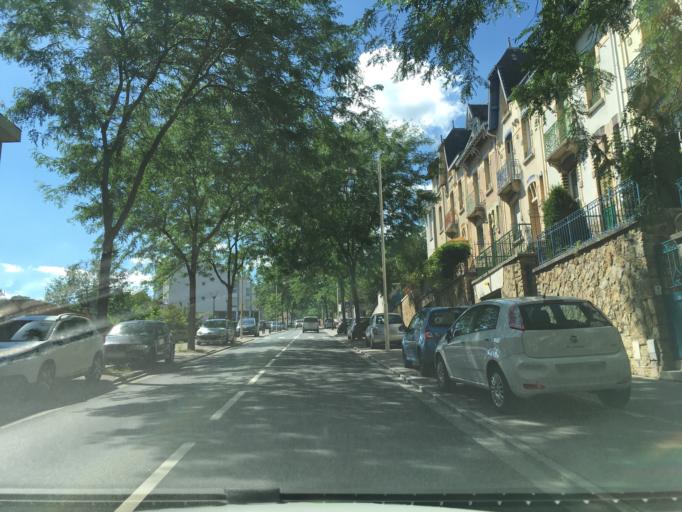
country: FR
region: Lorraine
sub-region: Departement de Meurthe-et-Moselle
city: Laxou
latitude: 48.6906
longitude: 6.1553
